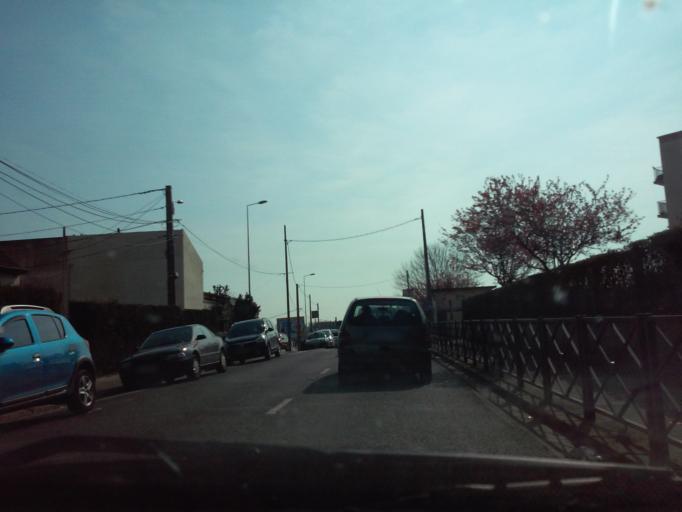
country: FR
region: Haute-Normandie
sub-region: Departement de la Seine-Maritime
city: Le Havre
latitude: 49.5124
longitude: 0.1294
